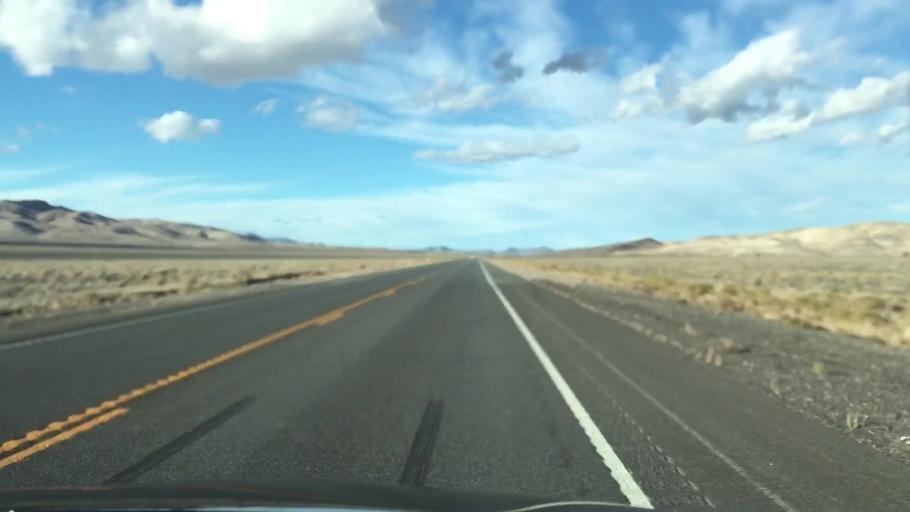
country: US
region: Nevada
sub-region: Esmeralda County
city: Goldfield
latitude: 37.5068
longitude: -117.1859
